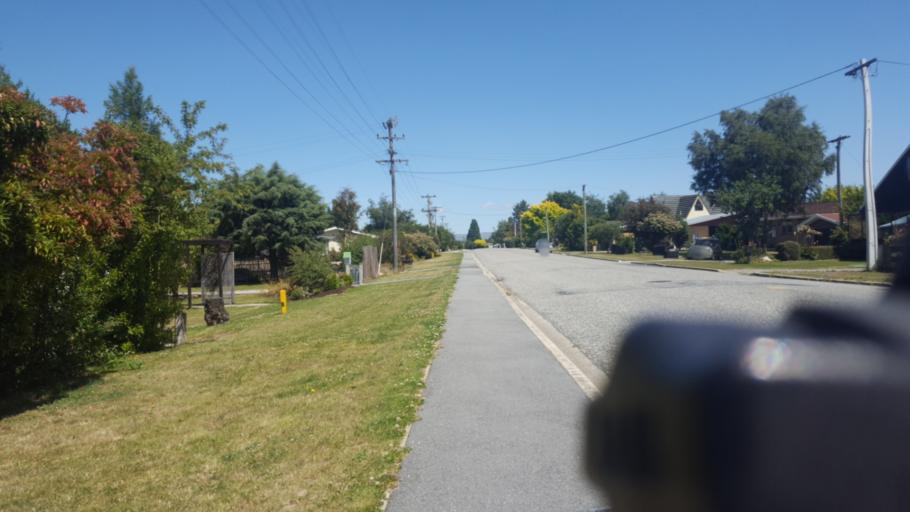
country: NZ
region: Otago
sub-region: Dunedin City
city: Dunedin
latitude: -45.1268
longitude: 170.1105
